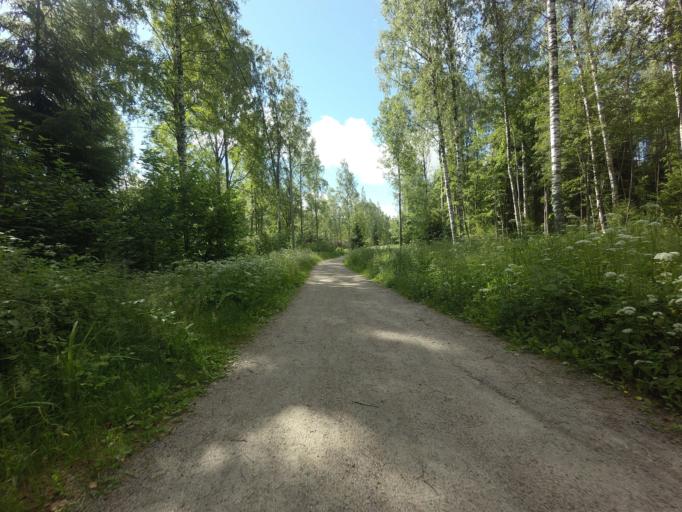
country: FI
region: Uusimaa
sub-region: Helsinki
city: Espoo
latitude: 60.1775
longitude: 24.6456
